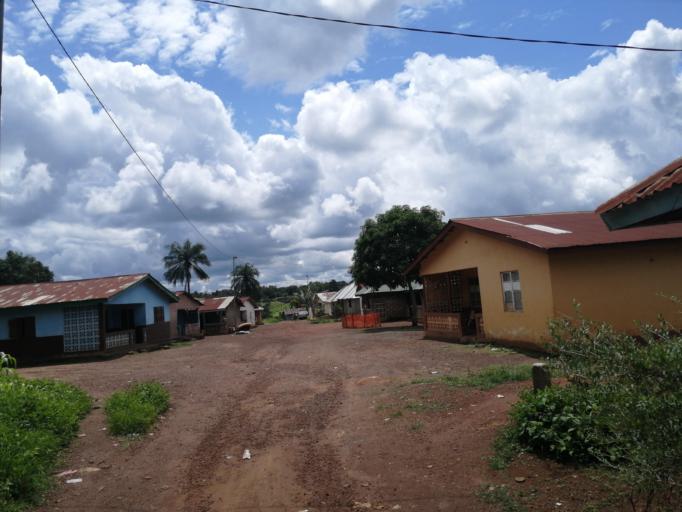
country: SL
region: Northern Province
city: Port Loko
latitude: 8.7709
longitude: -12.7789
